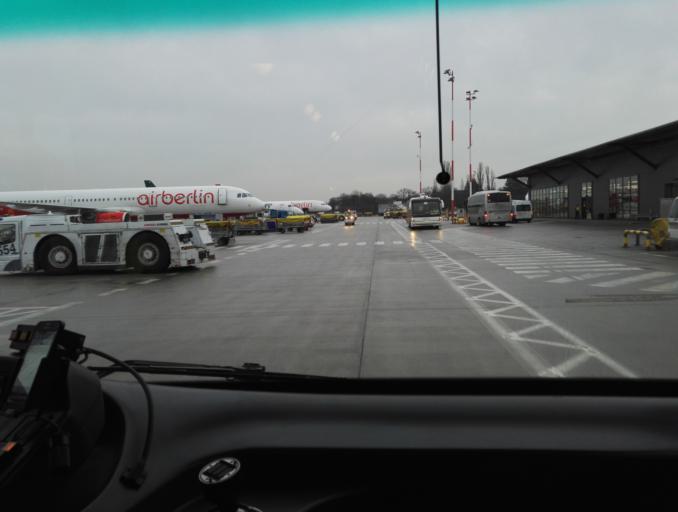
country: DE
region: Berlin
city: Tegel
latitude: 52.5562
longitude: 13.2967
